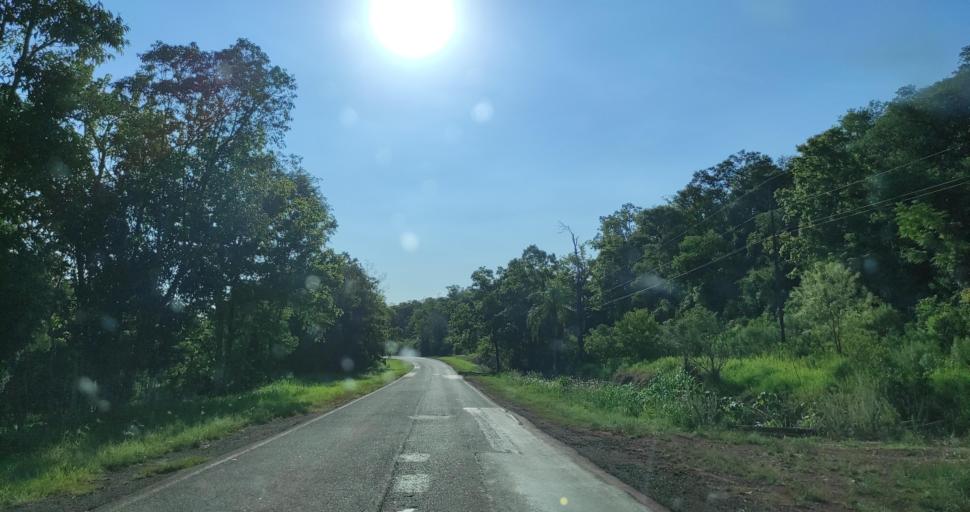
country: AR
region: Misiones
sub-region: Departamento de Eldorado
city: Eldorado
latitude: -26.4004
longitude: -54.4216
